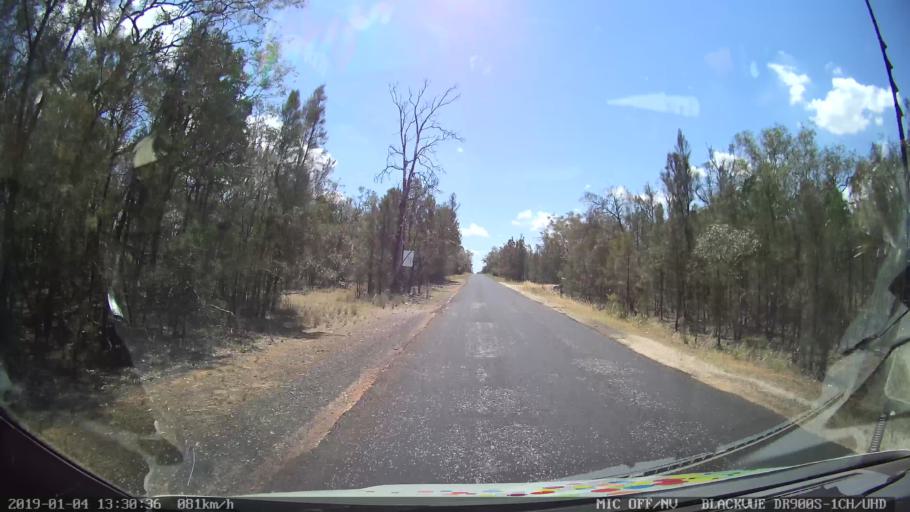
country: AU
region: New South Wales
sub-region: Parkes
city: Peak Hill
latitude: -32.6330
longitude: 148.5494
